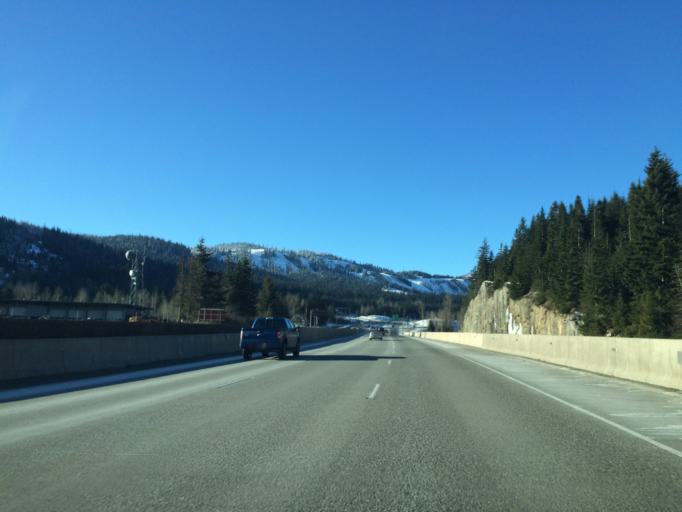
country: US
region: Washington
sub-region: King County
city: Tanner
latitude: 47.3919
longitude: -121.3859
